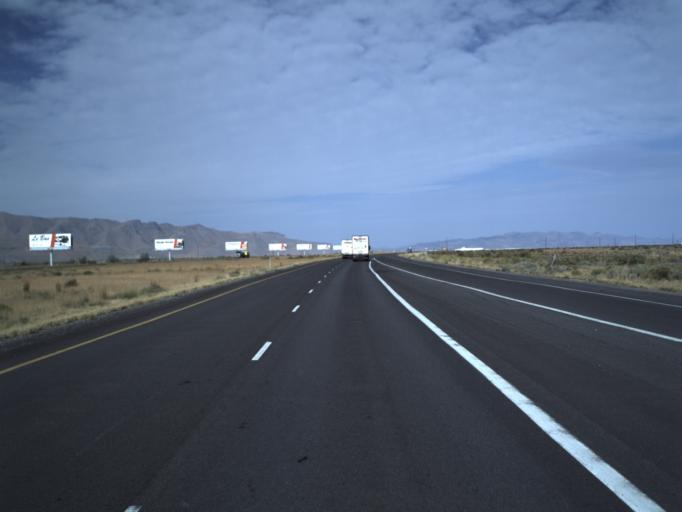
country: US
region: Utah
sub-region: Tooele County
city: Grantsville
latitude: 40.6863
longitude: -112.4491
